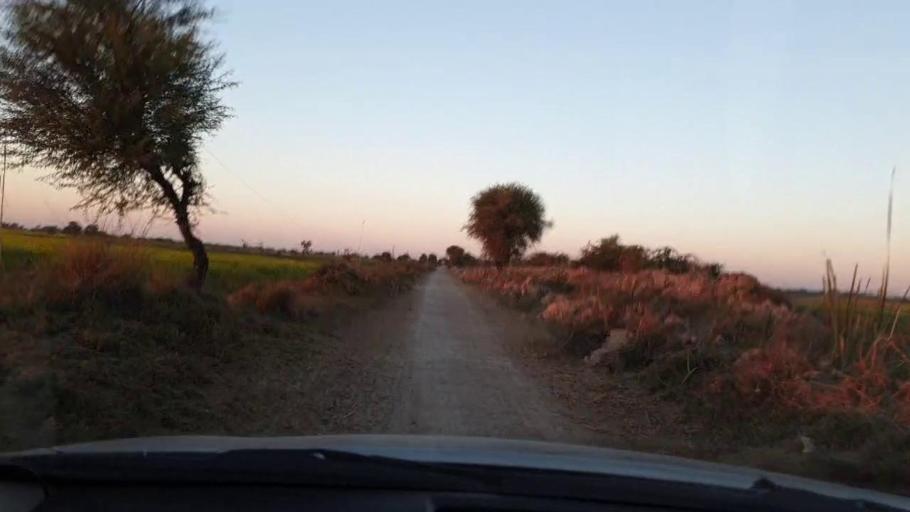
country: PK
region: Sindh
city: Jhol
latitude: 25.9067
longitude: 68.8858
